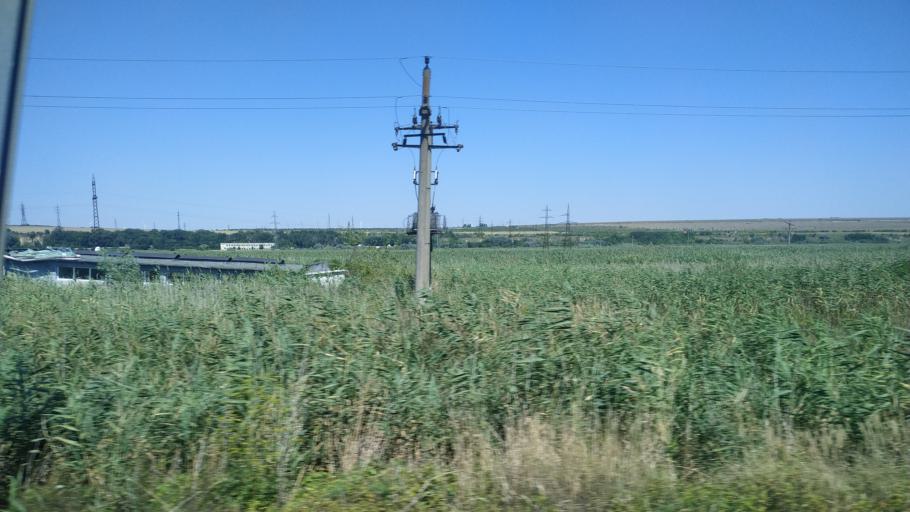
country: RO
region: Constanta
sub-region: Comuna Mircea Voda
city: Satu Nou
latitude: 44.2619
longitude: 28.1970
